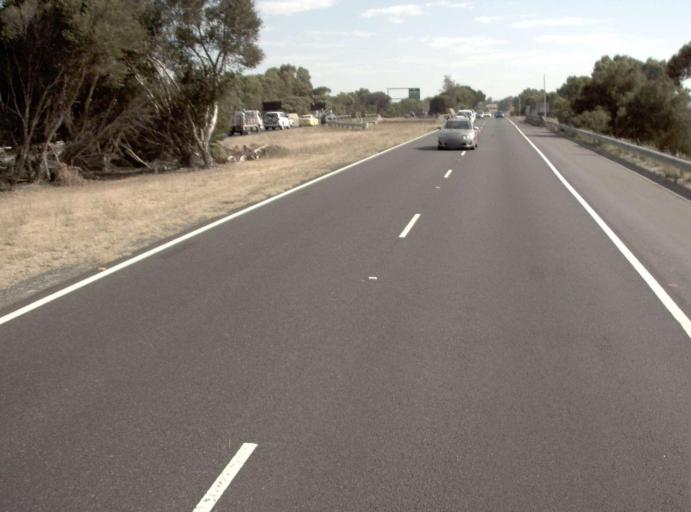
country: AU
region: Victoria
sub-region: Casey
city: Eumemmerring
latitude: -38.0139
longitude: 145.2500
